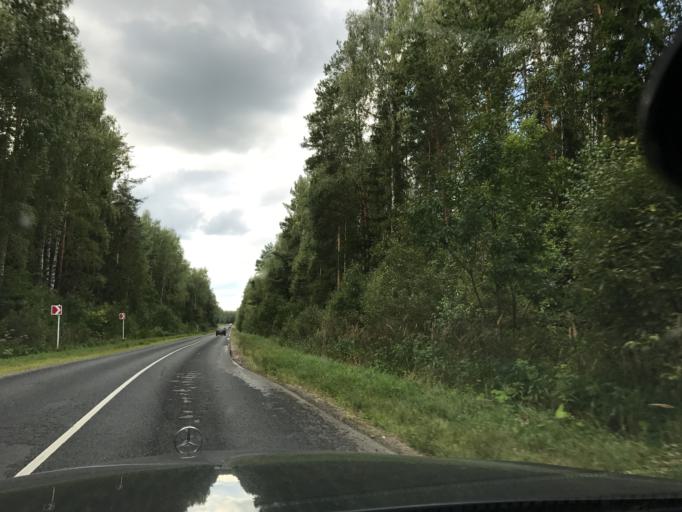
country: RU
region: Vladimir
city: Raduzhnyy
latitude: 55.9847
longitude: 40.2558
